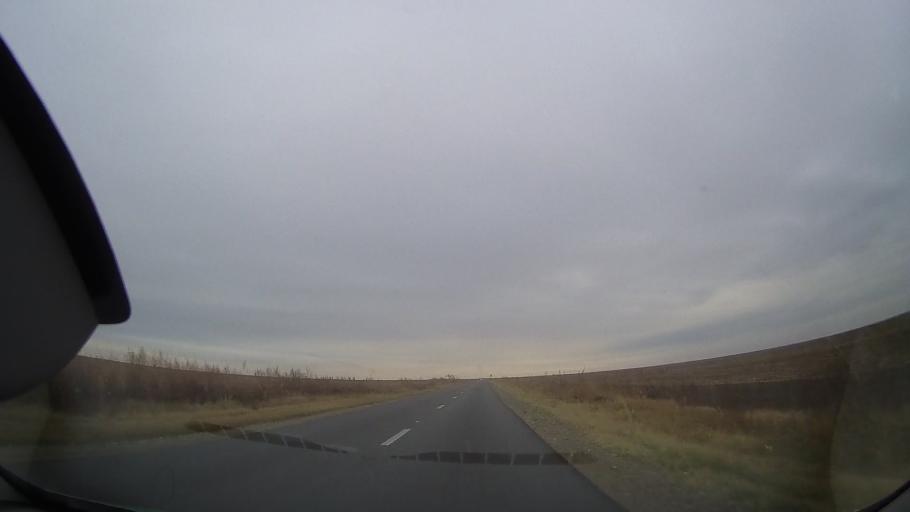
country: RO
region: Ialomita
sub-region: Oras Amara
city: Amara
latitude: 44.6450
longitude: 27.3005
